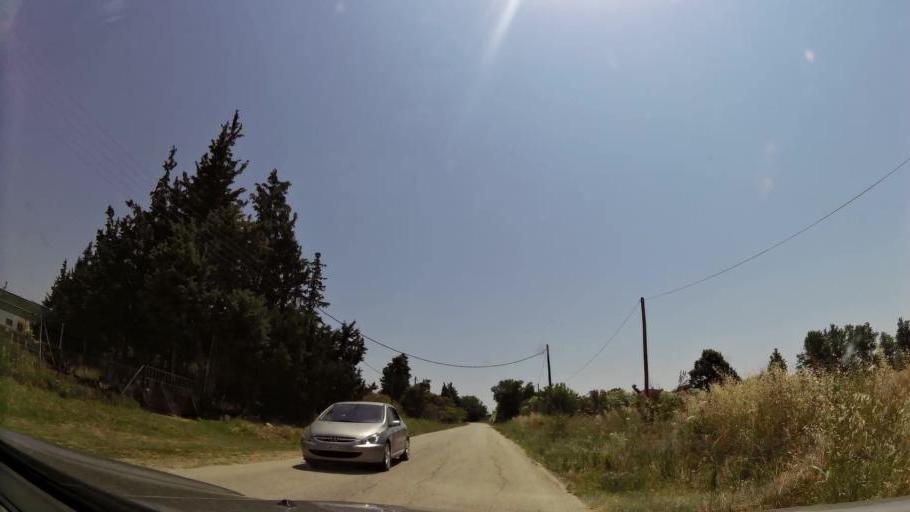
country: GR
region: Central Macedonia
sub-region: Nomos Thessalonikis
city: Nea Michaniona
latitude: 40.4738
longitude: 22.8727
